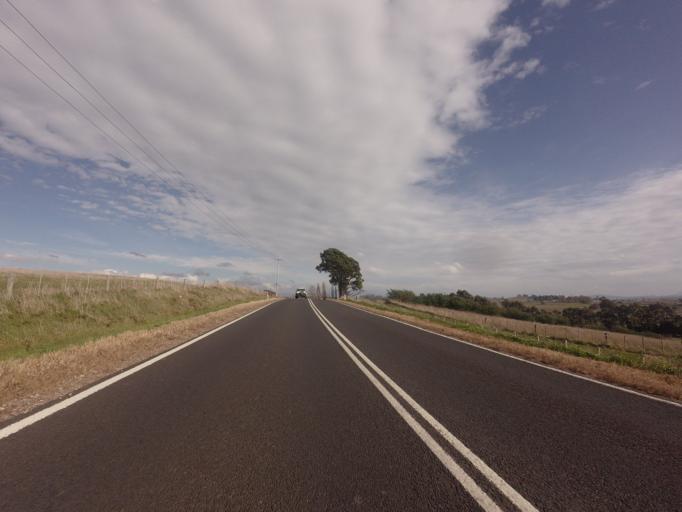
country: AU
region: Tasmania
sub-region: Meander Valley
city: Deloraine
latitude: -41.5200
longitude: 146.7214
